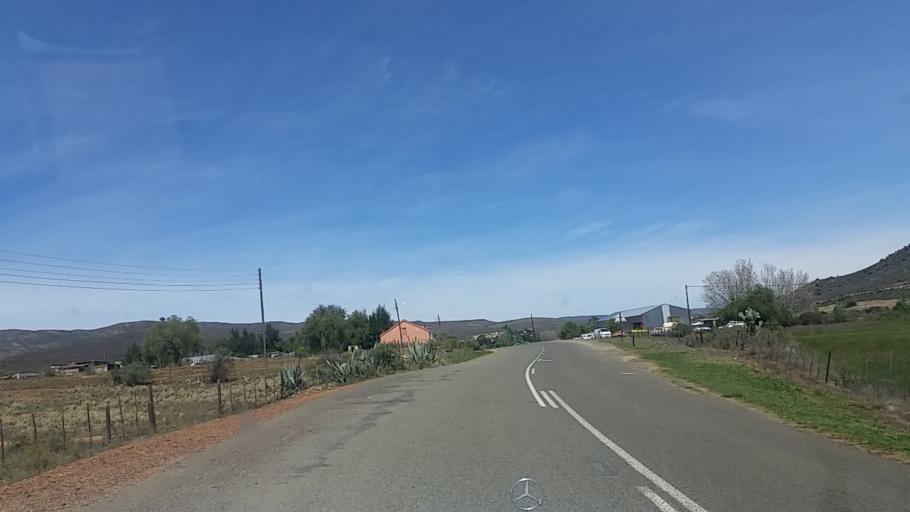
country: ZA
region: Western Cape
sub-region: Eden District Municipality
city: Knysna
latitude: -33.6442
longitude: 23.1380
